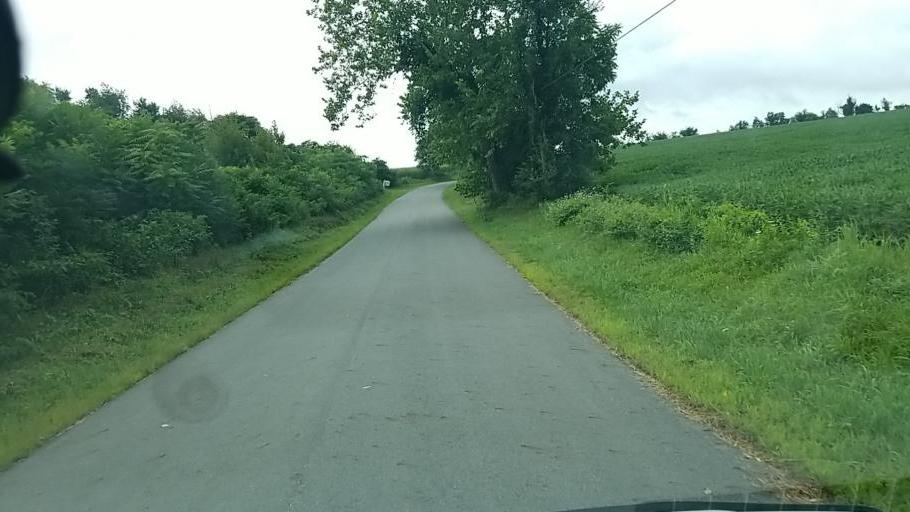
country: US
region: Pennsylvania
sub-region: Dauphin County
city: Elizabethville
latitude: 40.5173
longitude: -76.8846
